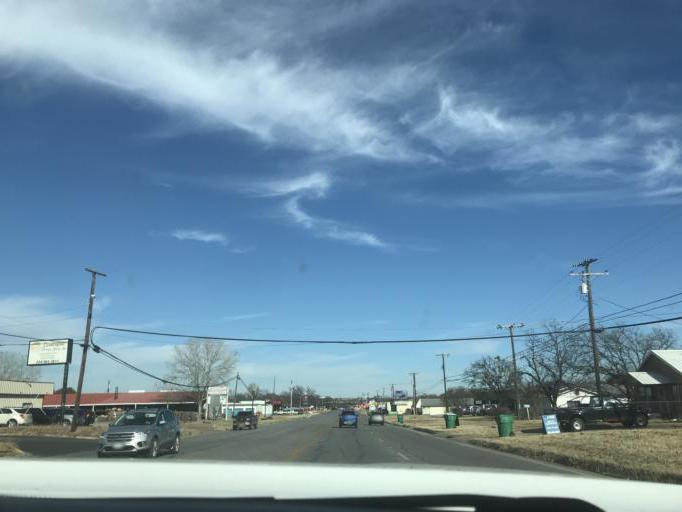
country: US
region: Texas
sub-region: Erath County
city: Stephenville
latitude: 32.2299
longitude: -98.2144
